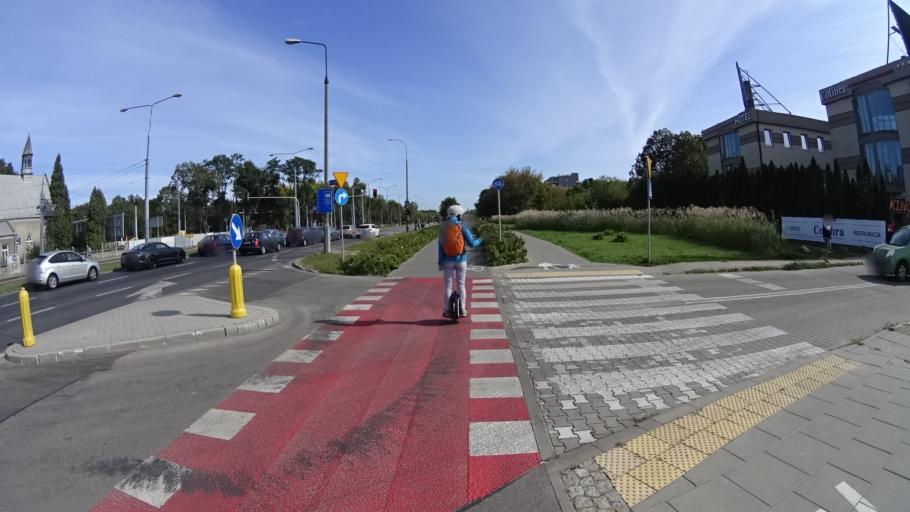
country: PL
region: Masovian Voivodeship
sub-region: Warszawa
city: Bemowo
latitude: 52.2234
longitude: 20.9319
